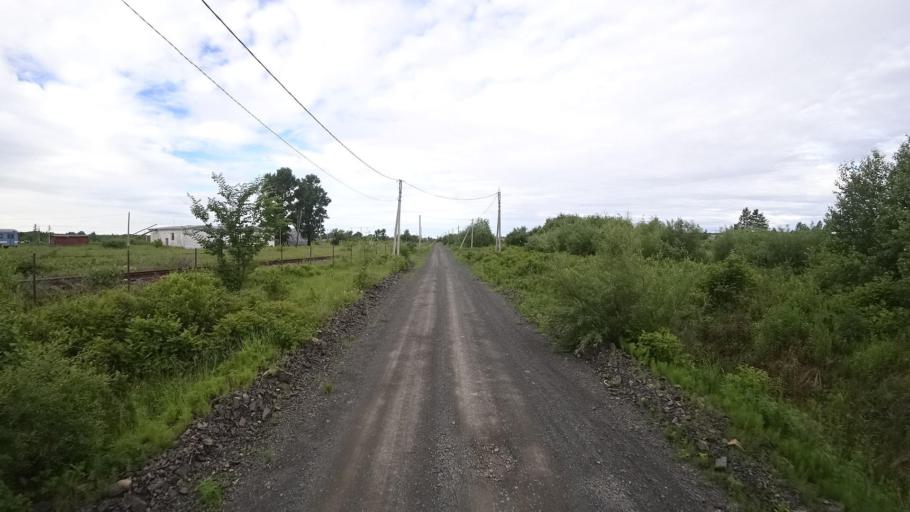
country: RU
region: Khabarovsk Krai
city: Amursk
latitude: 49.9070
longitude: 136.1470
